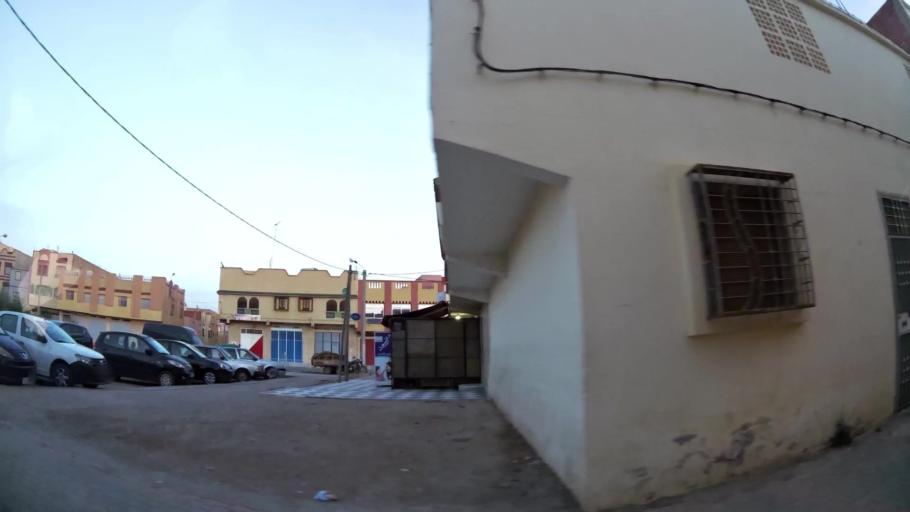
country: MA
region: Oriental
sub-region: Oujda-Angad
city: Oujda
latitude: 34.6797
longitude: -1.8786
